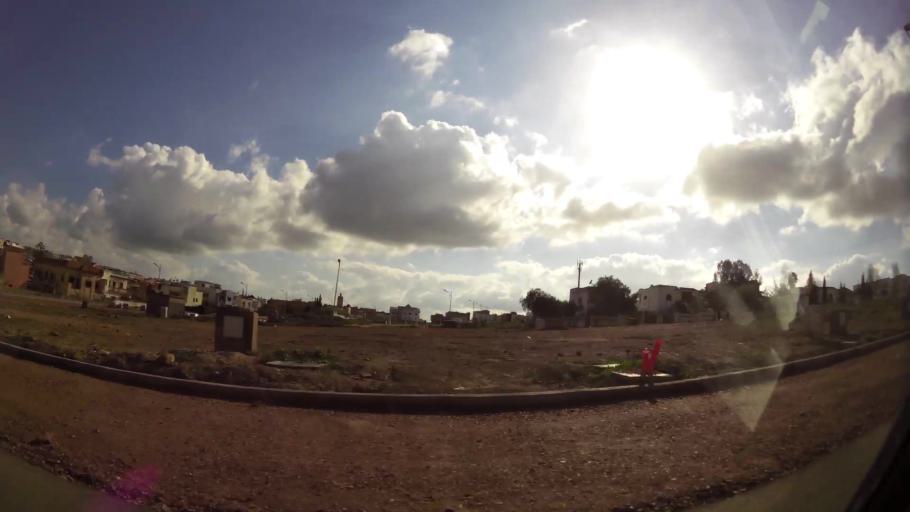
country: MA
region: Chaouia-Ouardigha
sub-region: Settat Province
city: Settat
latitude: 33.0108
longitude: -7.6345
